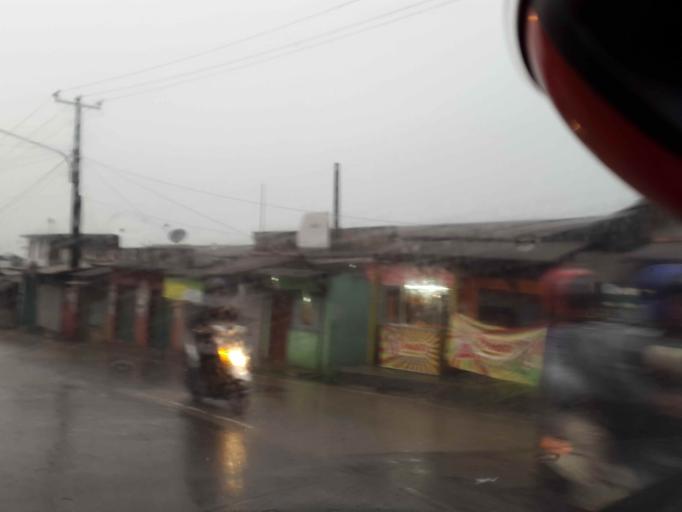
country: ID
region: West Java
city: Margahayukencana
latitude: -6.9525
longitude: 107.5237
